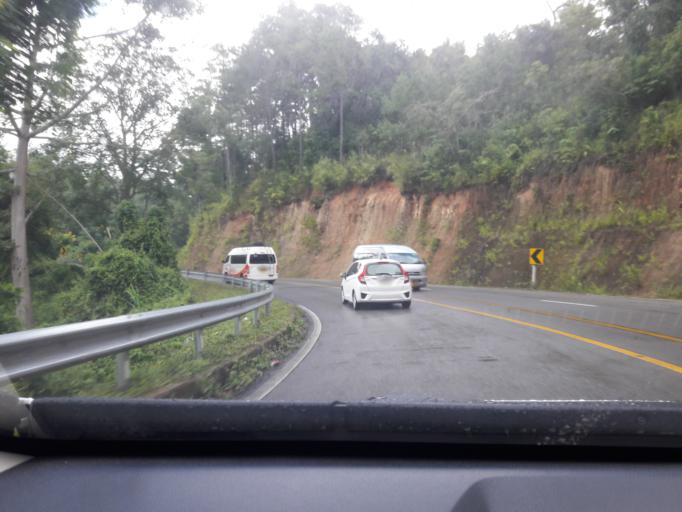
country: TH
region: Mae Hong Son
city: Mae Hi
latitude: 19.2303
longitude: 98.6707
